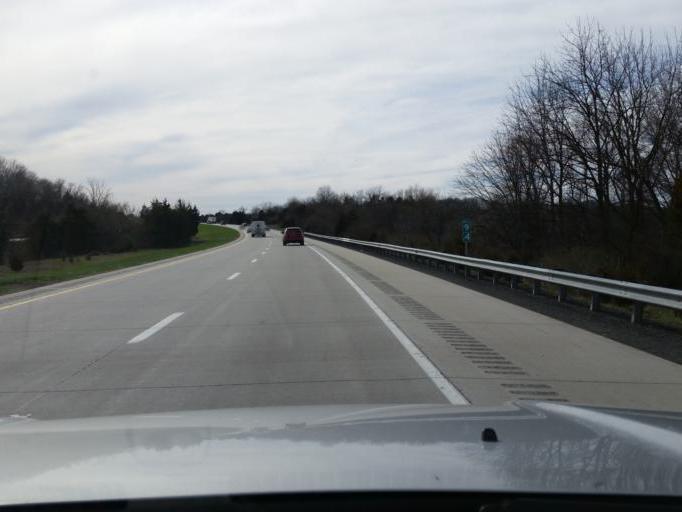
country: US
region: Pennsylvania
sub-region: Lancaster County
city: Elizabethtown
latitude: 40.1941
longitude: -76.6371
